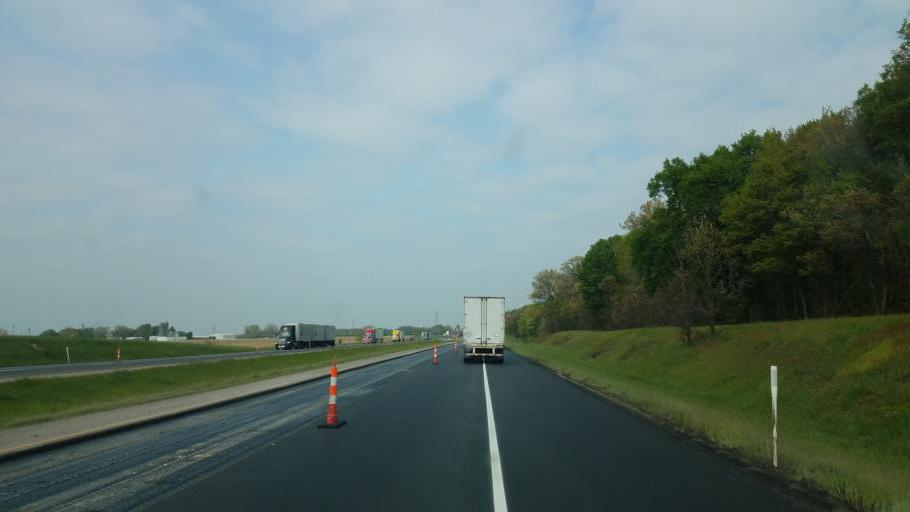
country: US
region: Indiana
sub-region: Saint Joseph County
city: Granger
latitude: 41.7339
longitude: -86.1152
